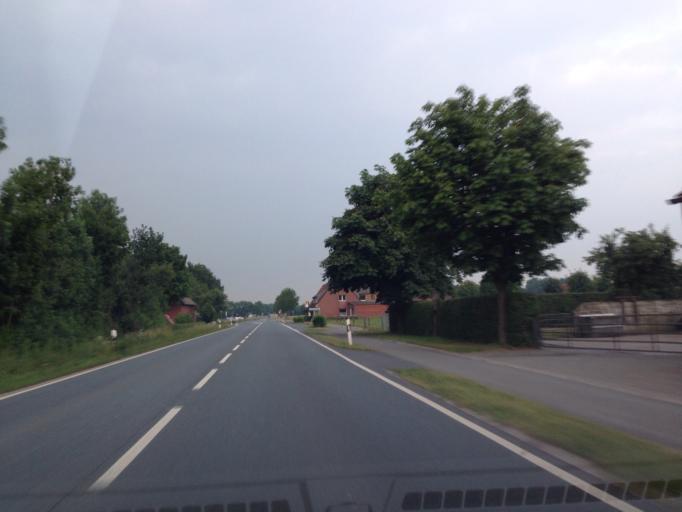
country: DE
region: North Rhine-Westphalia
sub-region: Regierungsbezirk Munster
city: Nottuln
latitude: 51.9138
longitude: 7.3903
